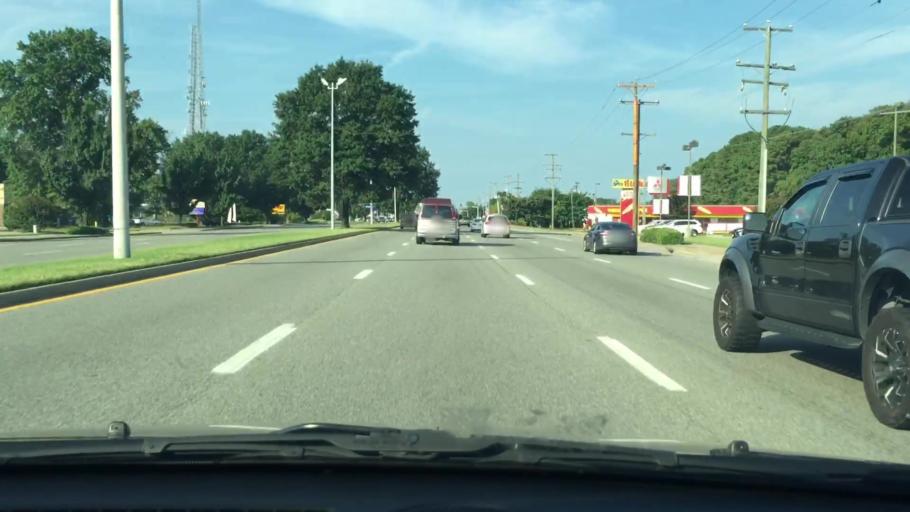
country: US
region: Virginia
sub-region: City of Newport News
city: Newport News
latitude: 37.0264
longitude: -76.4305
